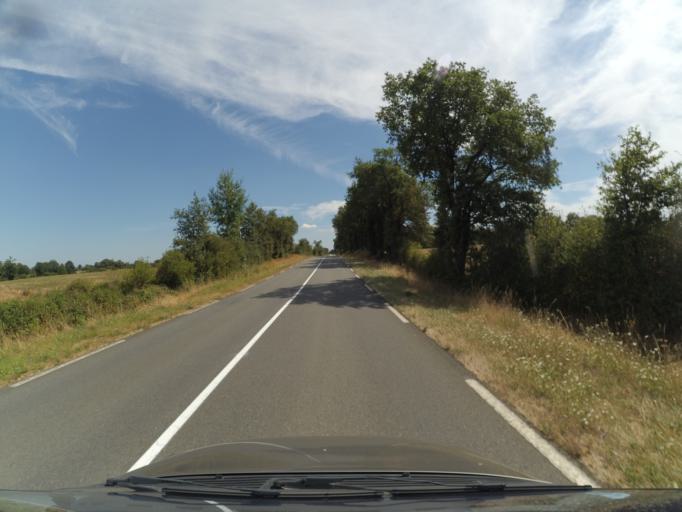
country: FR
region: Poitou-Charentes
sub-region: Departement de la Charente
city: Confolens
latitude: 46.0467
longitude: 0.6218
